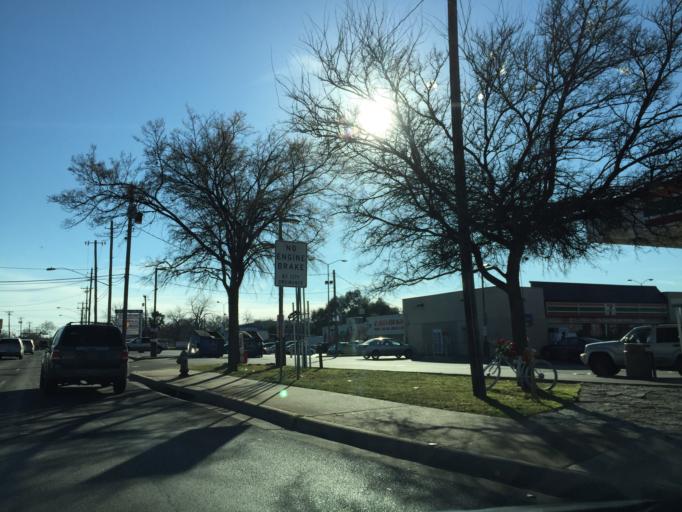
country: US
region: Texas
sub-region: Travis County
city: Austin
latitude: 30.2262
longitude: -97.7698
